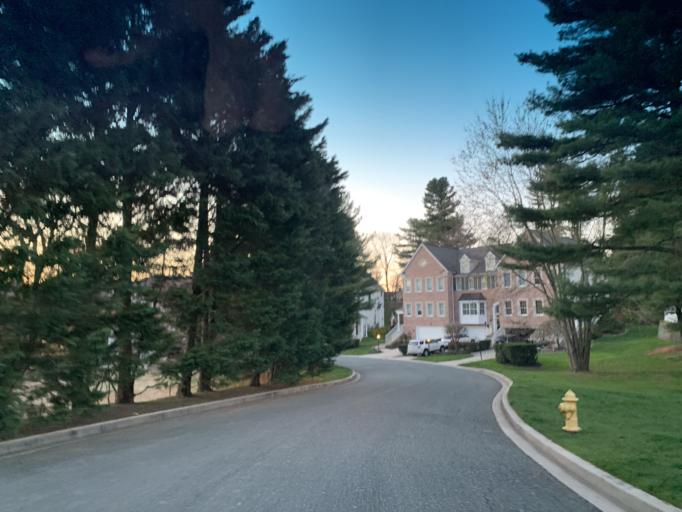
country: US
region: Maryland
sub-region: Harford County
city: Bel Air South
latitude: 39.5056
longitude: -76.3323
